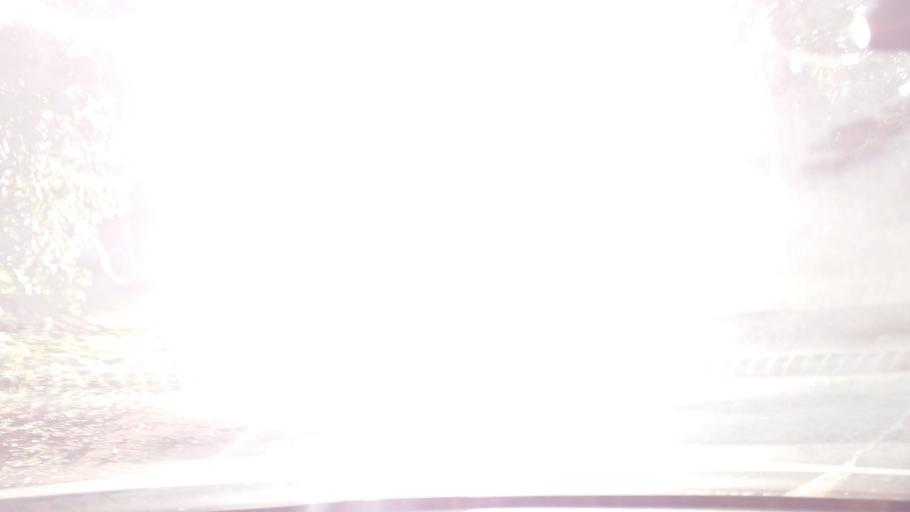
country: BR
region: Sao Paulo
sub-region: Franco Da Rocha
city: Franco da Rocha
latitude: -23.3339
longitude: -46.6873
